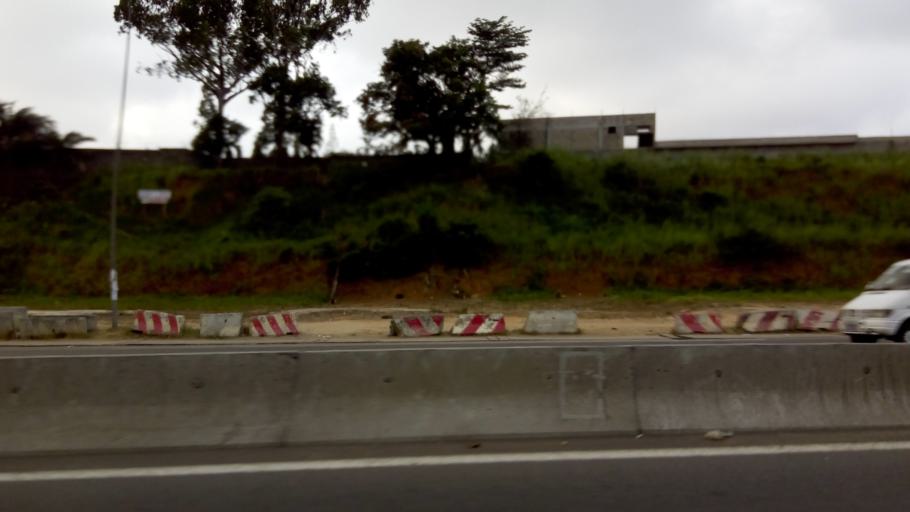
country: CI
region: Lagunes
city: Abidjan
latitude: 5.3526
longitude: -3.9805
